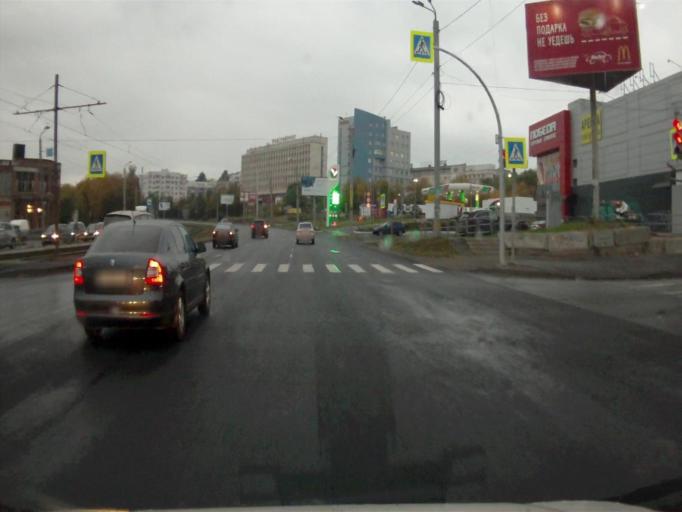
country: RU
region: Chelyabinsk
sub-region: Gorod Chelyabinsk
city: Chelyabinsk
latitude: 55.1881
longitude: 61.3607
